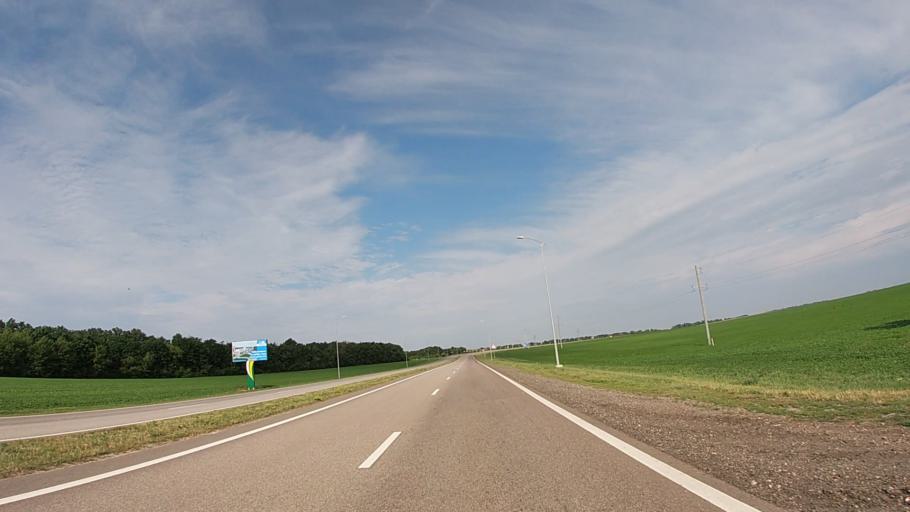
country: RU
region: Belgorod
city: Rakitnoye
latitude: 50.7903
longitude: 35.8771
